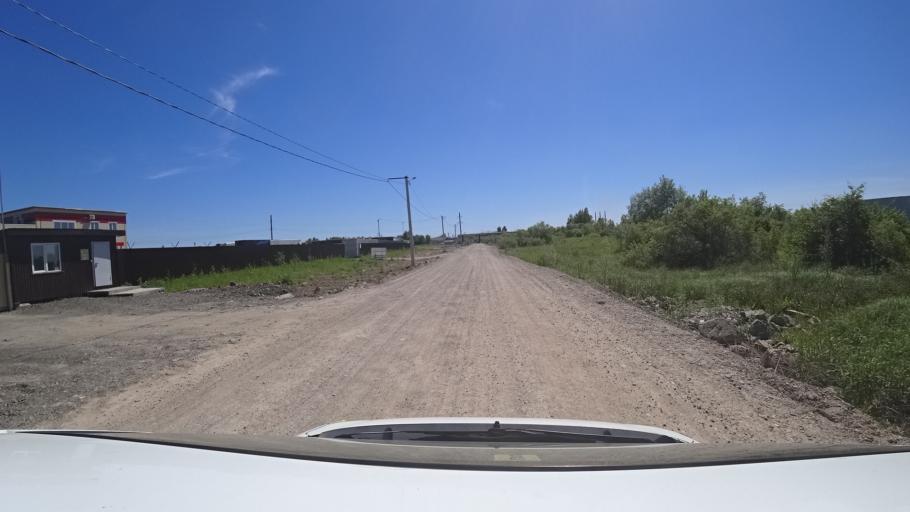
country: RU
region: Khabarovsk Krai
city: Topolevo
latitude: 48.4773
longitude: 135.1723
